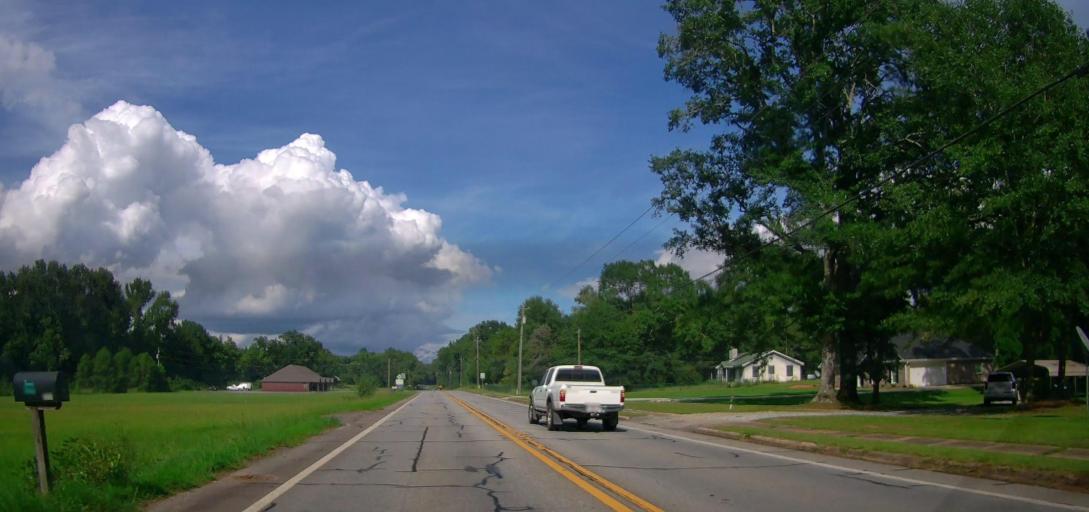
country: US
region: Georgia
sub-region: Harris County
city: Hamilton
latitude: 32.6430
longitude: -84.8823
